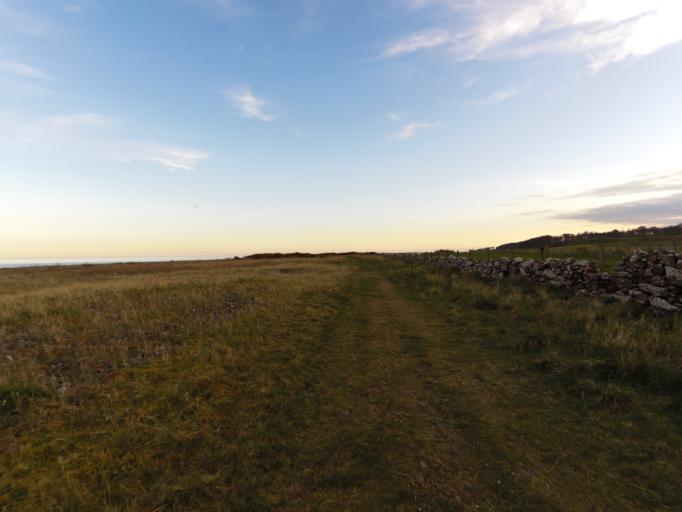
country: GB
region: Scotland
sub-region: Aberdeenshire
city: Inverbervie
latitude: 56.8145
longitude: -2.3031
